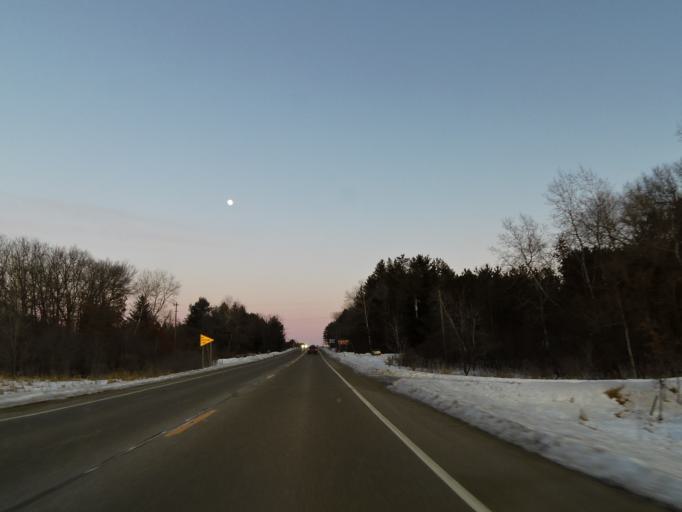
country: US
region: Minnesota
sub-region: Washington County
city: Grant
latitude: 45.0795
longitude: -92.8695
